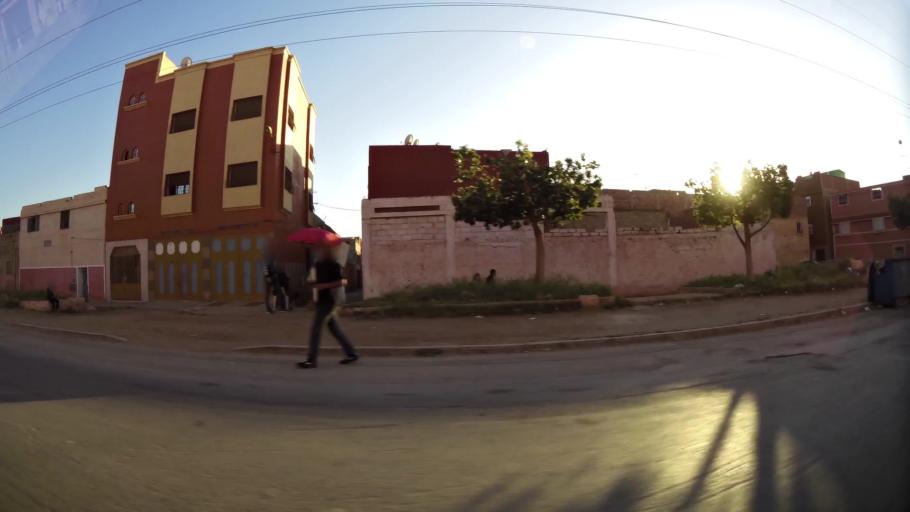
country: MA
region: Oriental
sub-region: Berkane-Taourirt
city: Berkane
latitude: 34.9229
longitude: -2.3122
